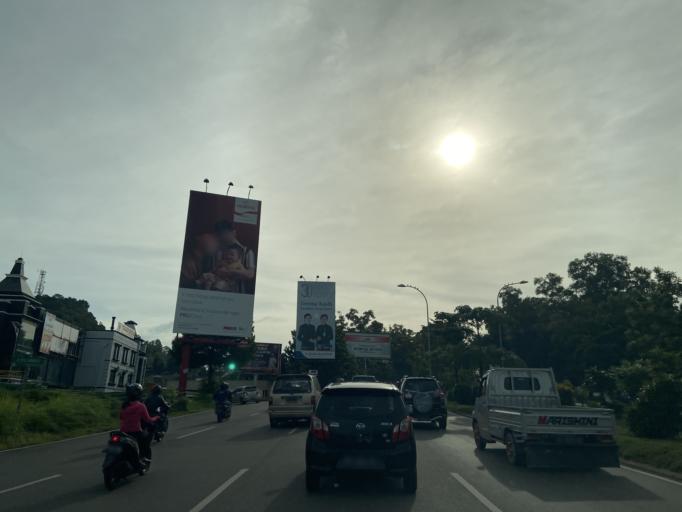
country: SG
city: Singapore
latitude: 1.1314
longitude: 104.0180
